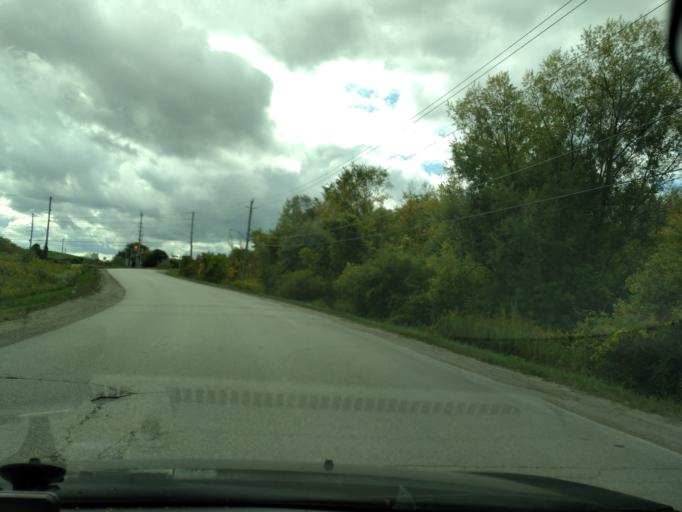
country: CA
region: Ontario
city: Bradford West Gwillimbury
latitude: 44.1300
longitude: -79.5572
